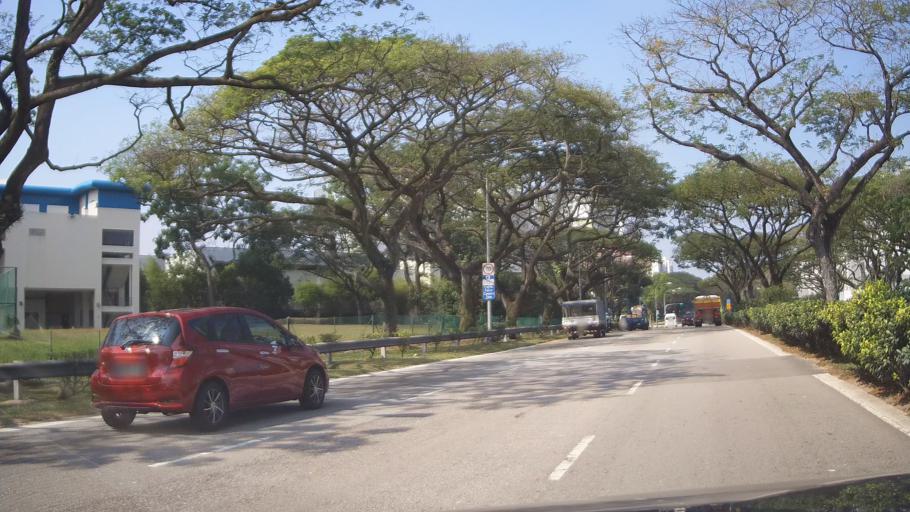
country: MY
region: Johor
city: Johor Bahru
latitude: 1.3528
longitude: 103.7136
